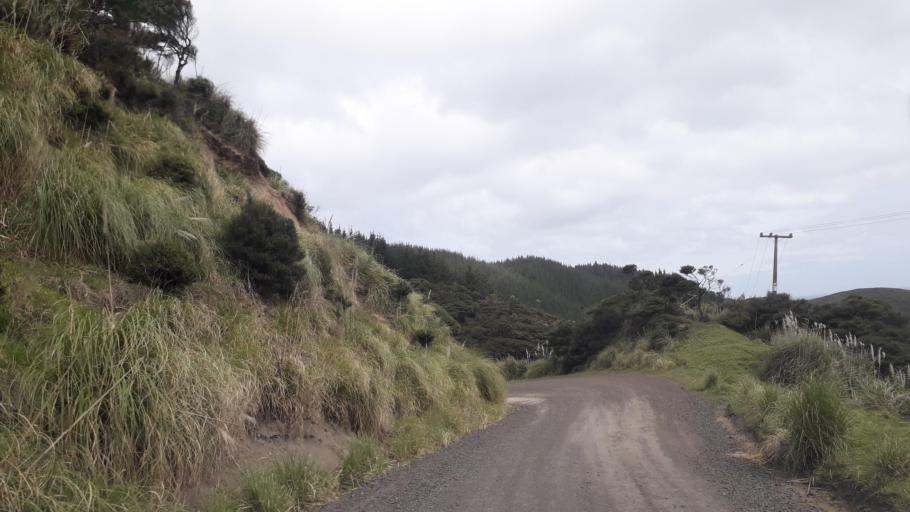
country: NZ
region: Northland
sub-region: Far North District
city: Ahipara
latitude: -35.4404
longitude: 173.3039
